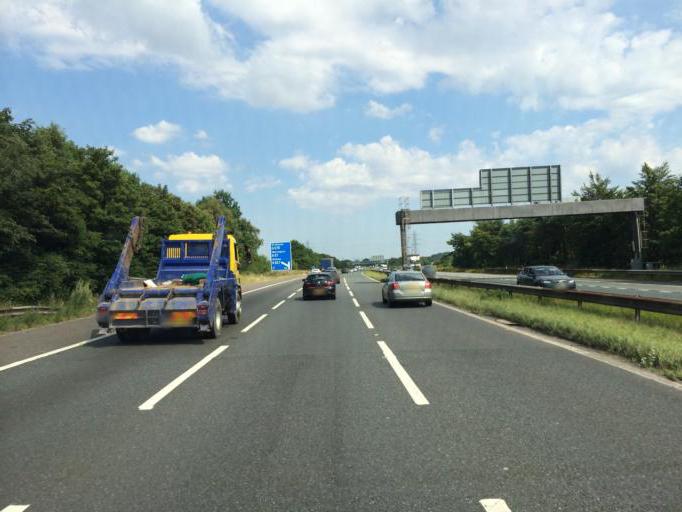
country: GB
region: England
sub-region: Knowsley
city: Whiston
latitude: 53.4016
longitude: -2.7863
